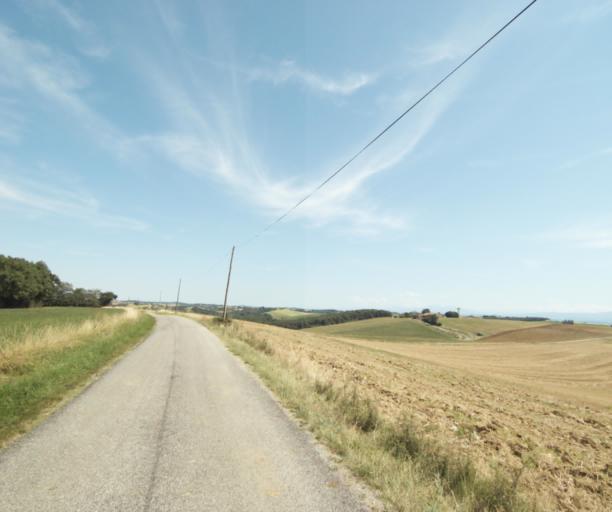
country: FR
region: Midi-Pyrenees
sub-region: Departement de la Haute-Garonne
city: Gaillac-Toulza
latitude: 43.2454
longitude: 1.4238
